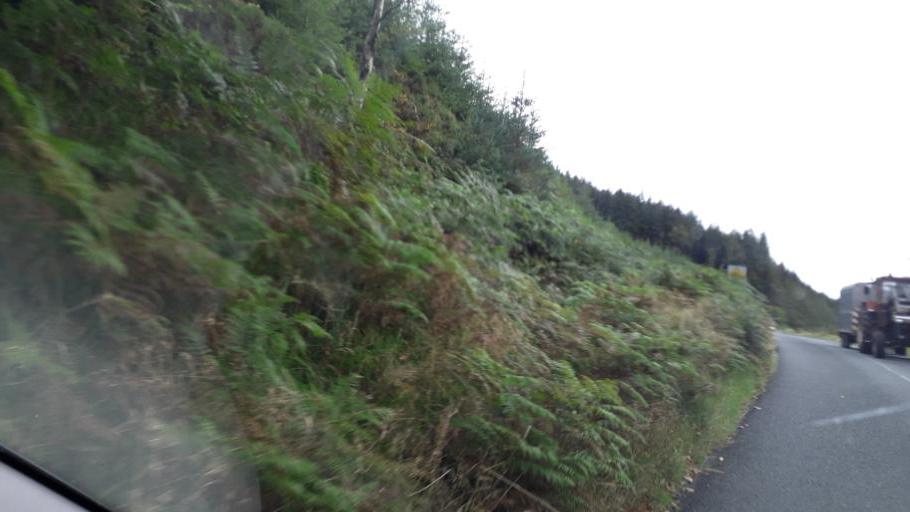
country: IE
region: Leinster
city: Ballinteer
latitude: 53.2390
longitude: -6.2872
